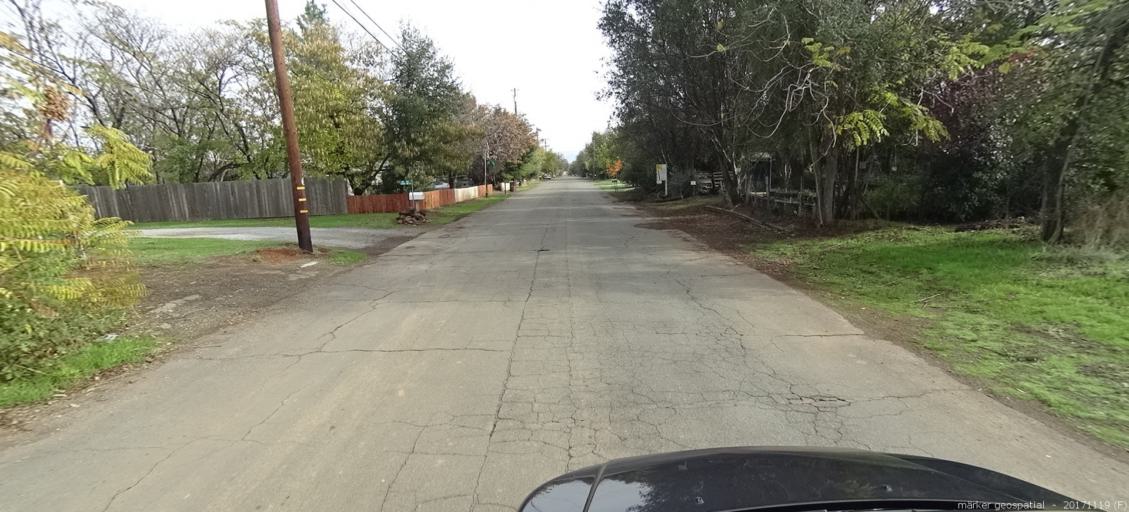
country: US
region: California
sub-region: Shasta County
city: Anderson
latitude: 40.4883
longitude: -122.2908
